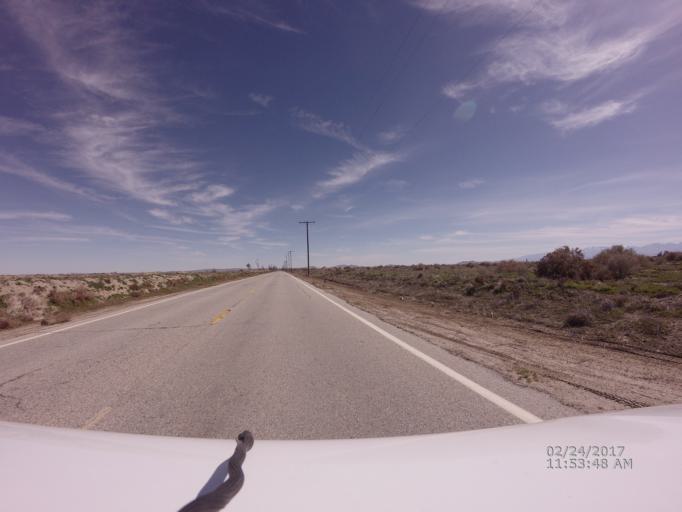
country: US
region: California
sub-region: Los Angeles County
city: Lancaster
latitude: 34.7191
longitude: -118.0395
